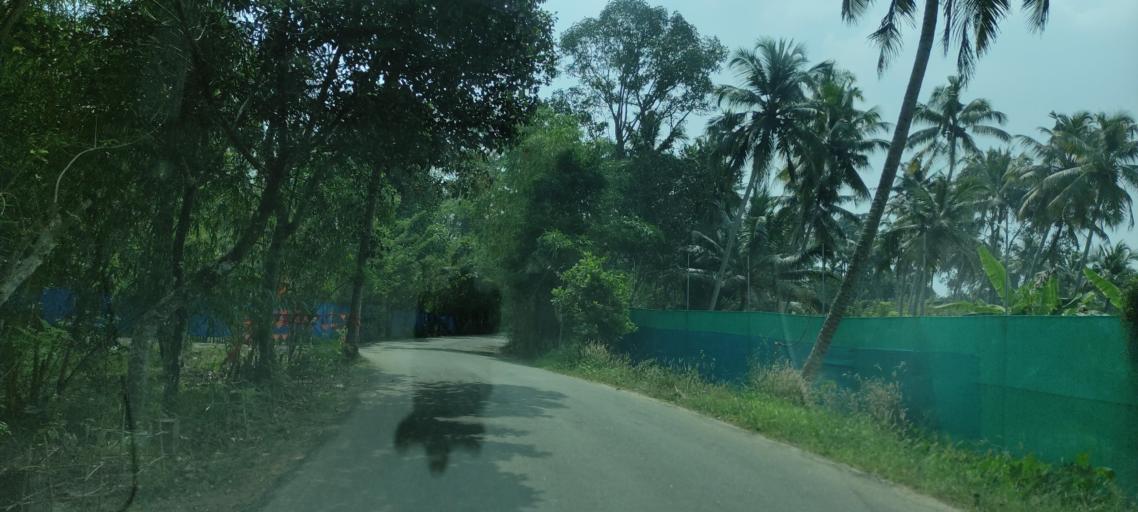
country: IN
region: Kerala
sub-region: Alappuzha
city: Shertallai
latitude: 9.6461
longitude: 76.3554
